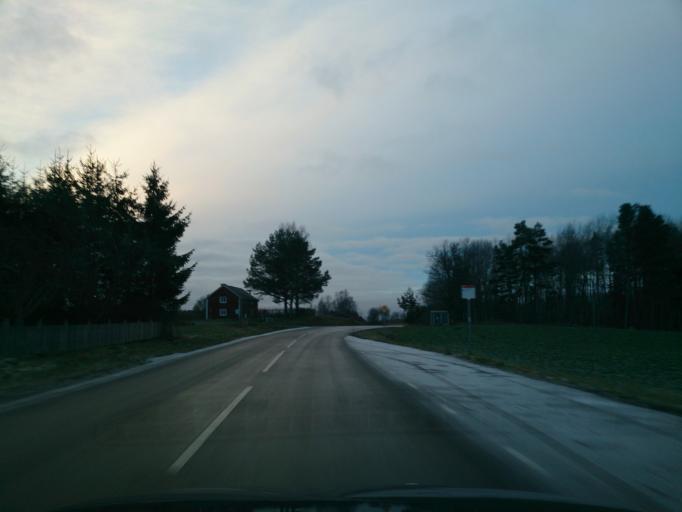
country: SE
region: OEstergoetland
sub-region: Norrkopings Kommun
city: Kimstad
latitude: 58.3927
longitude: 15.9688
